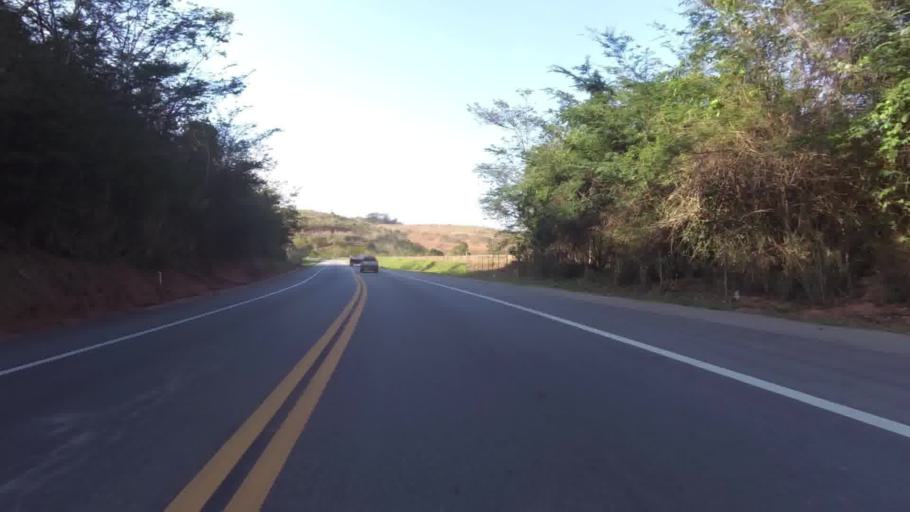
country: BR
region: Espirito Santo
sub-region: Mimoso Do Sul
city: Mimoso do Sul
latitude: -21.1897
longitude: -41.2940
